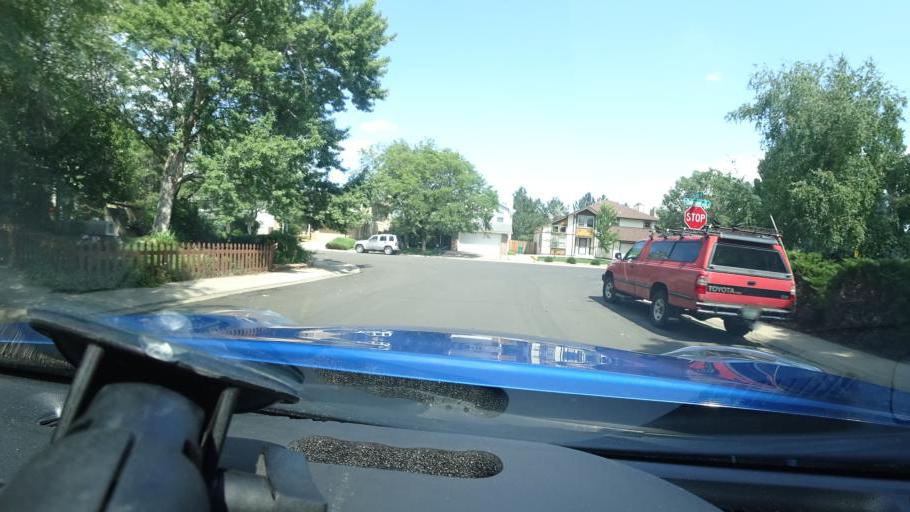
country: US
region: Colorado
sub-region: Adams County
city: Aurora
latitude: 39.6788
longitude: -104.8504
